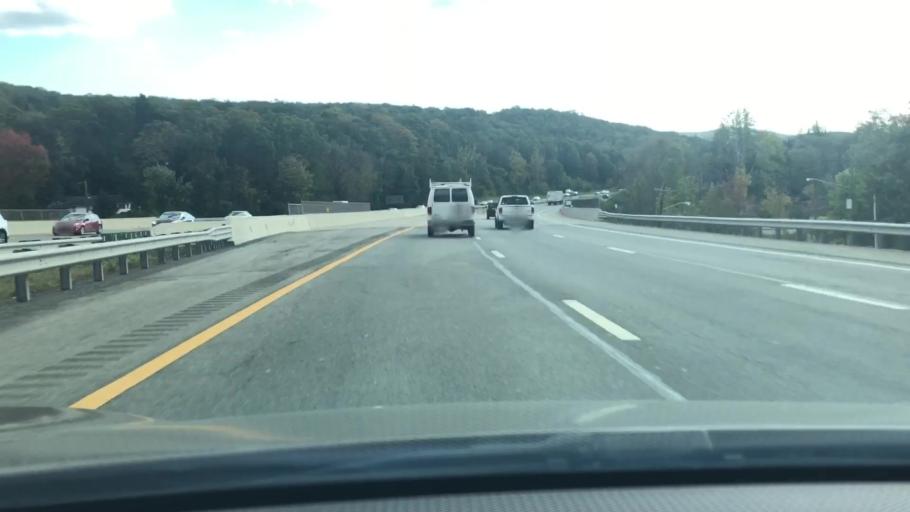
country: US
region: New York
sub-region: Rockland County
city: Sloatsburg
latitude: 41.1641
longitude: -74.1844
